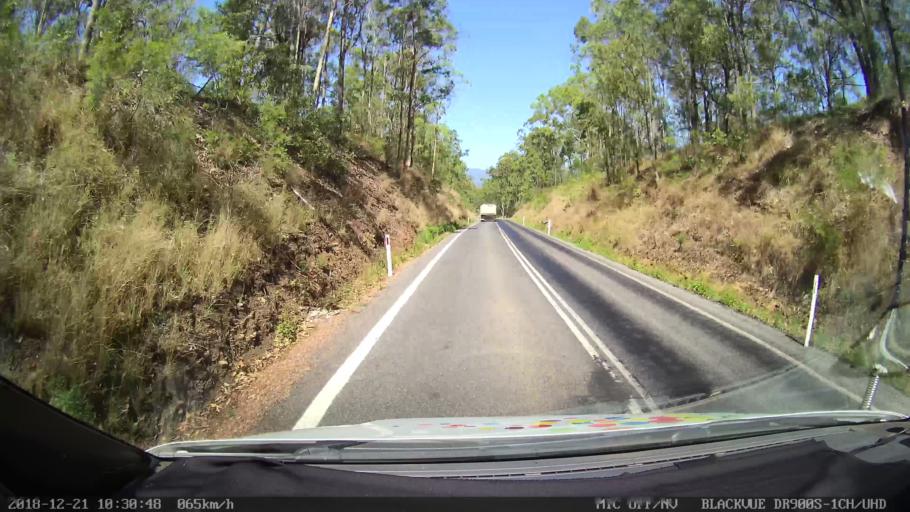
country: AU
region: New South Wales
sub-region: Clarence Valley
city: South Grafton
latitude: -29.6331
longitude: 152.7043
